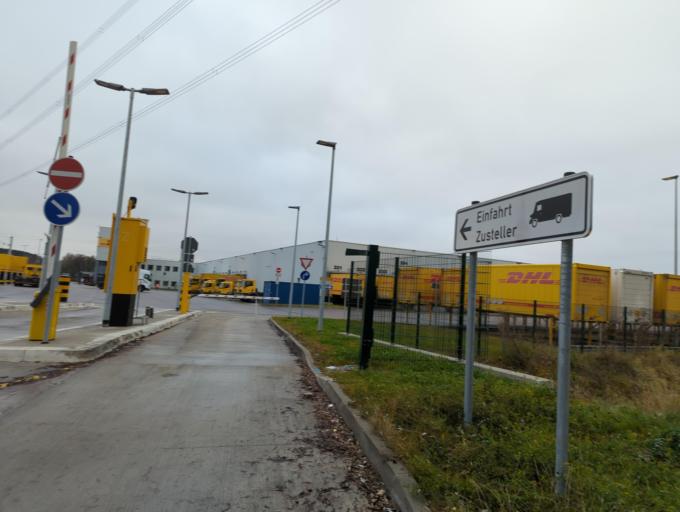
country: DE
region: Bavaria
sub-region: Swabia
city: Wasserburg
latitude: 48.4260
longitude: 10.2866
